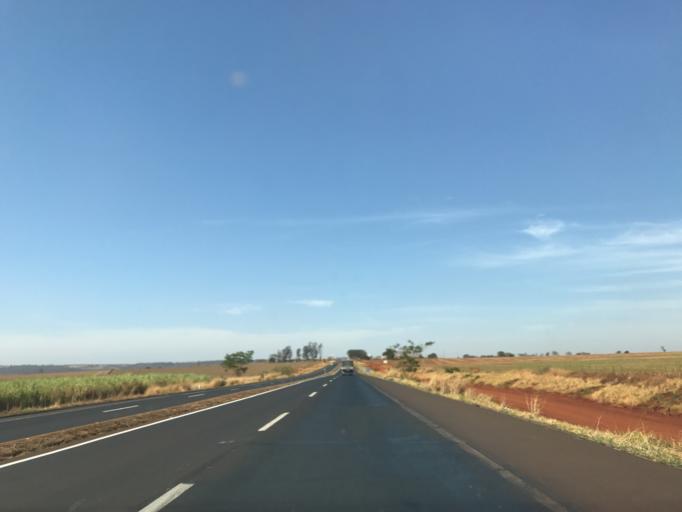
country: BR
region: Minas Gerais
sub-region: Centralina
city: Centralina
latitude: -18.5579
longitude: -49.1938
